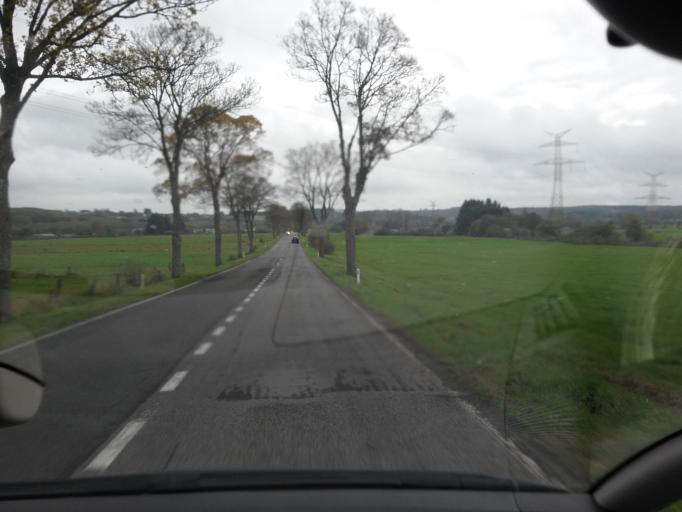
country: BE
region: Wallonia
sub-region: Province du Luxembourg
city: Attert
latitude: 49.7062
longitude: 5.7151
